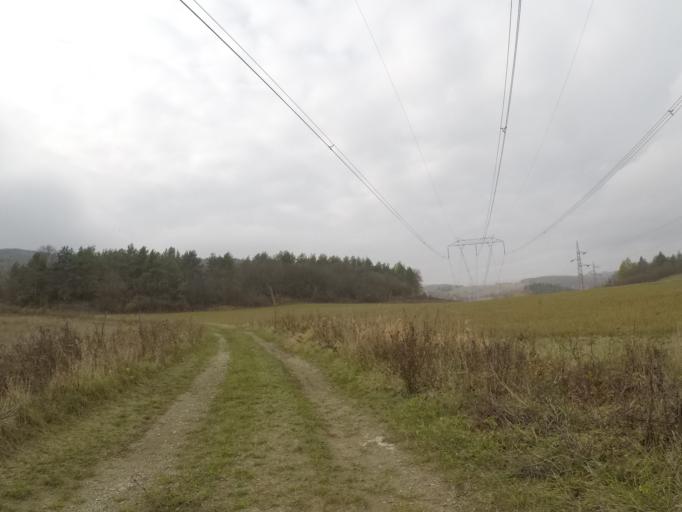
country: SK
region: Presovsky
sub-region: Okres Presov
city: Presov
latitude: 48.9050
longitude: 21.1774
